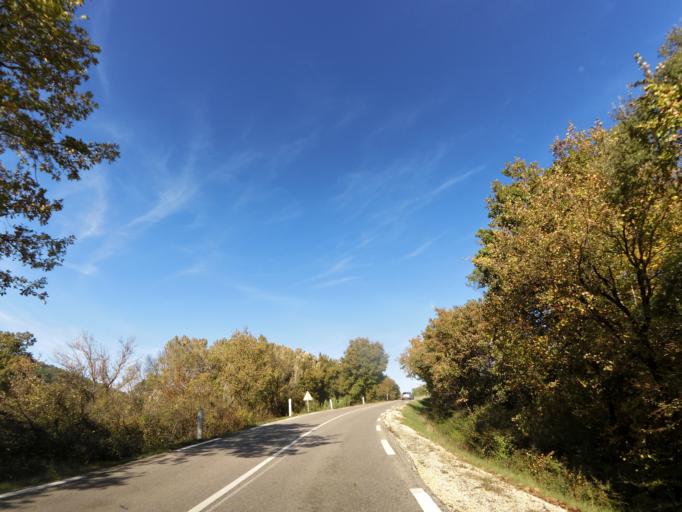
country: FR
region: Languedoc-Roussillon
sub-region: Departement du Gard
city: Ledignan
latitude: 43.9241
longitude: 4.1045
